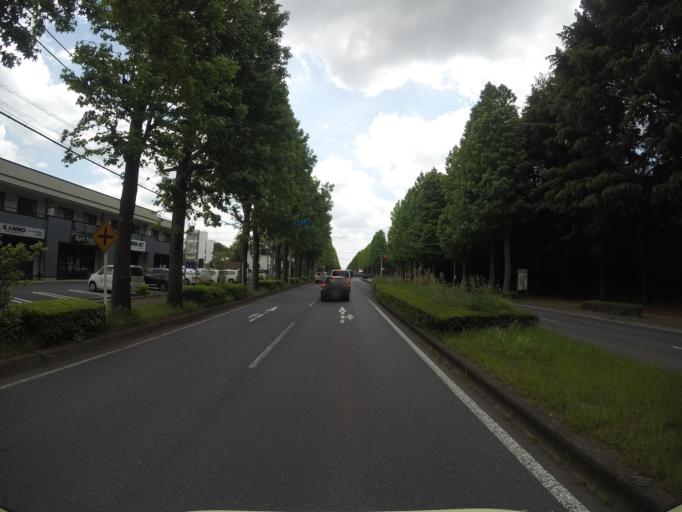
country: JP
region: Ibaraki
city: Naka
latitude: 36.0242
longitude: 140.1189
